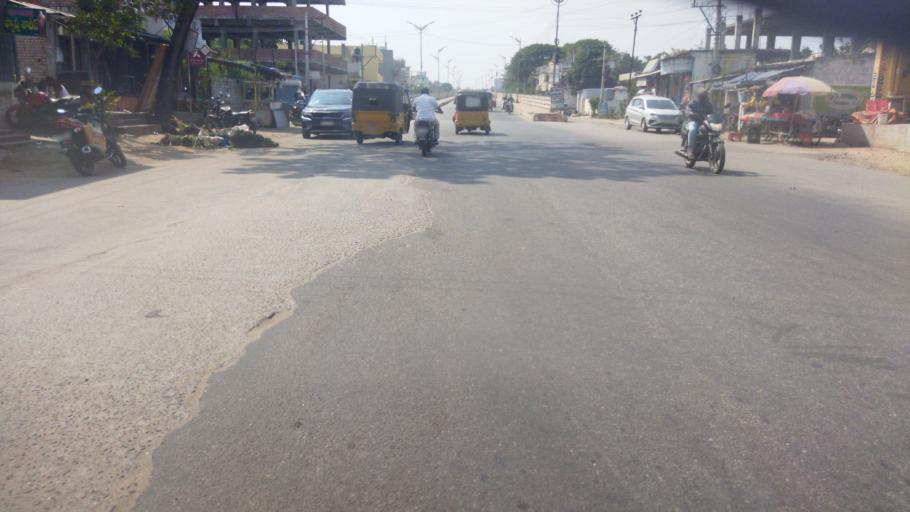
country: IN
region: Telangana
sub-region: Nalgonda
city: Nalgonda
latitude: 17.0686
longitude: 79.2820
